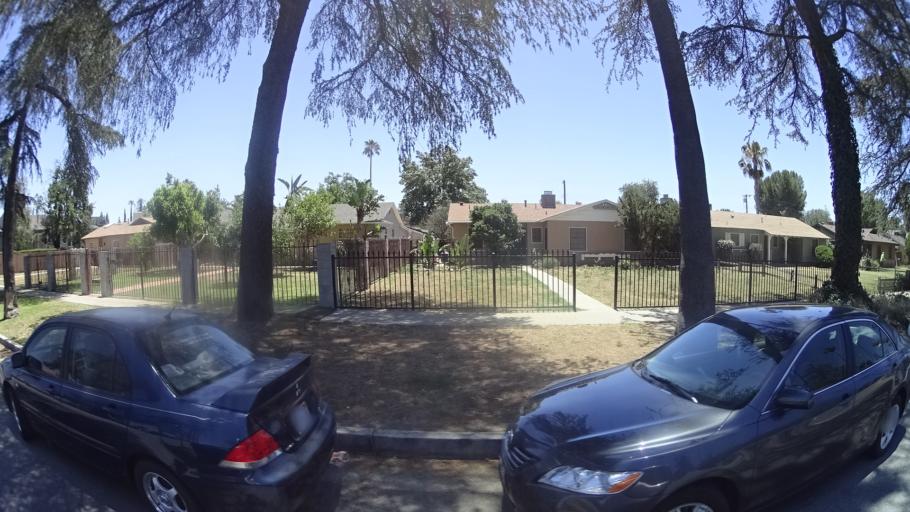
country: US
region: California
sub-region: Los Angeles County
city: Northridge
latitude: 34.2011
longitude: -118.5040
